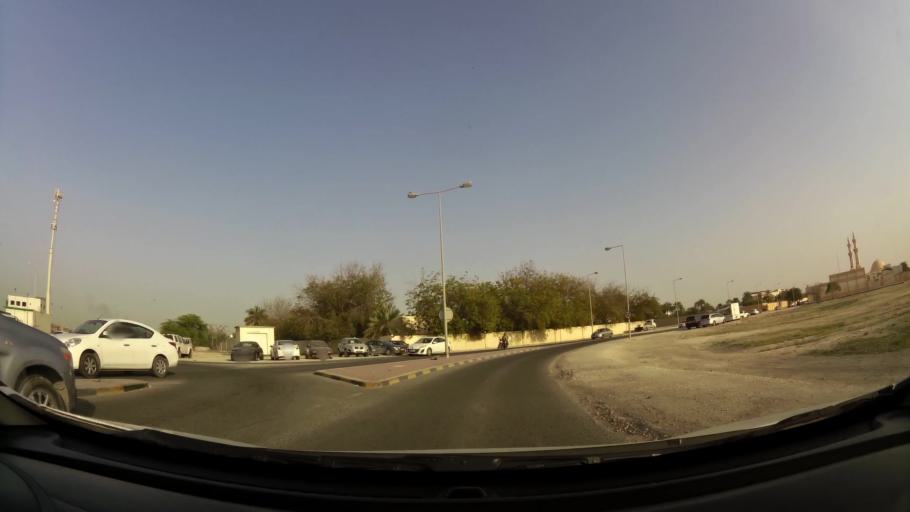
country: BH
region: Manama
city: Jidd Hafs
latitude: 26.2160
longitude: 50.4797
